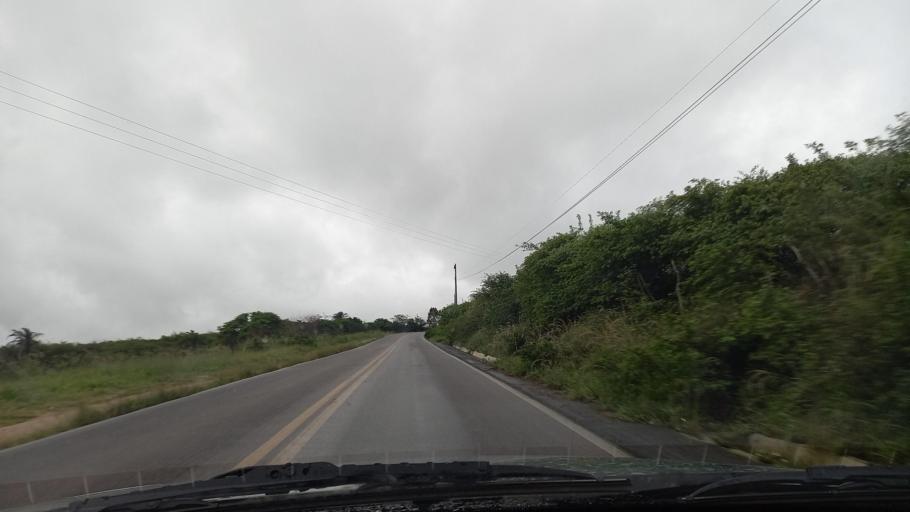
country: BR
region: Pernambuco
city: Garanhuns
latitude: -8.8489
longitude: -36.5182
